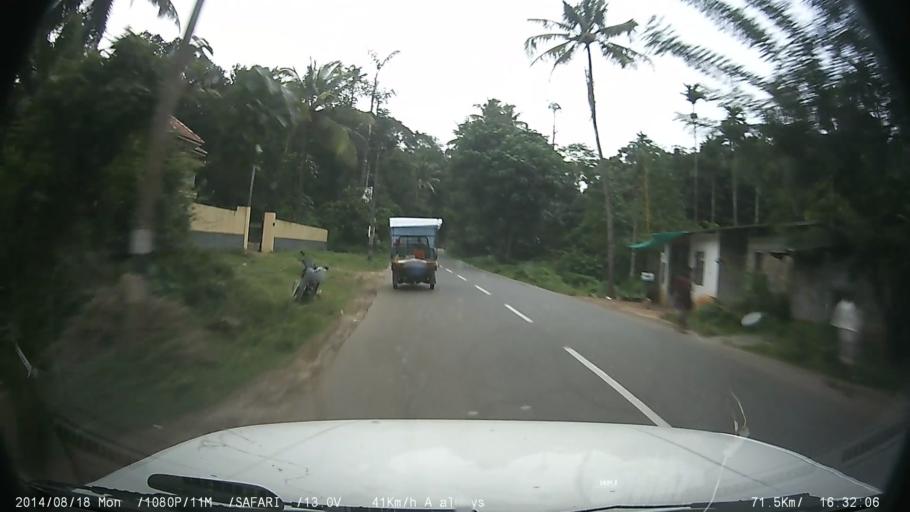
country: IN
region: Kerala
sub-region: Kottayam
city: Palackattumala
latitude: 9.8010
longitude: 76.5748
